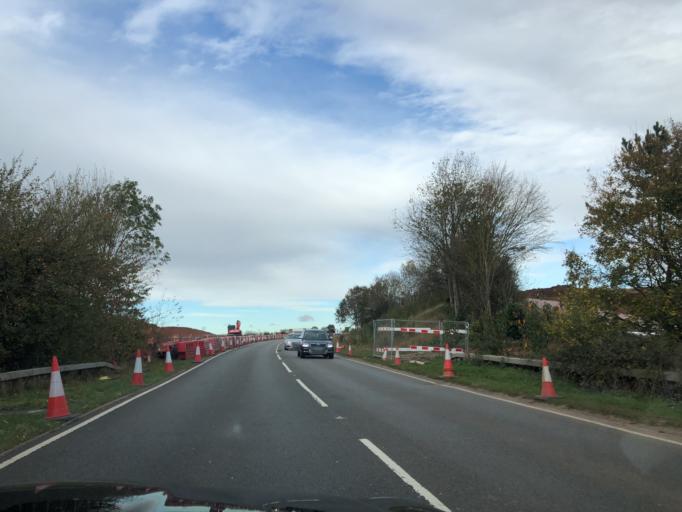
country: GB
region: England
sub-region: Warwickshire
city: Warwick
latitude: 52.2650
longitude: -1.5601
